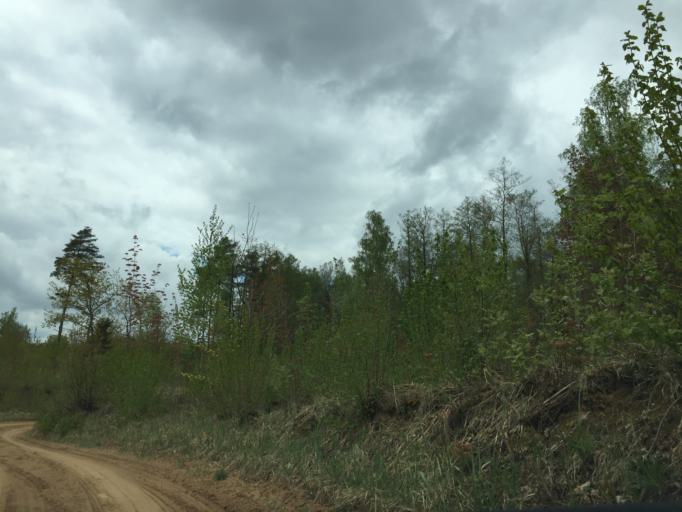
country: LV
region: Kekava
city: Kekava
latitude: 56.8009
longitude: 24.3012
